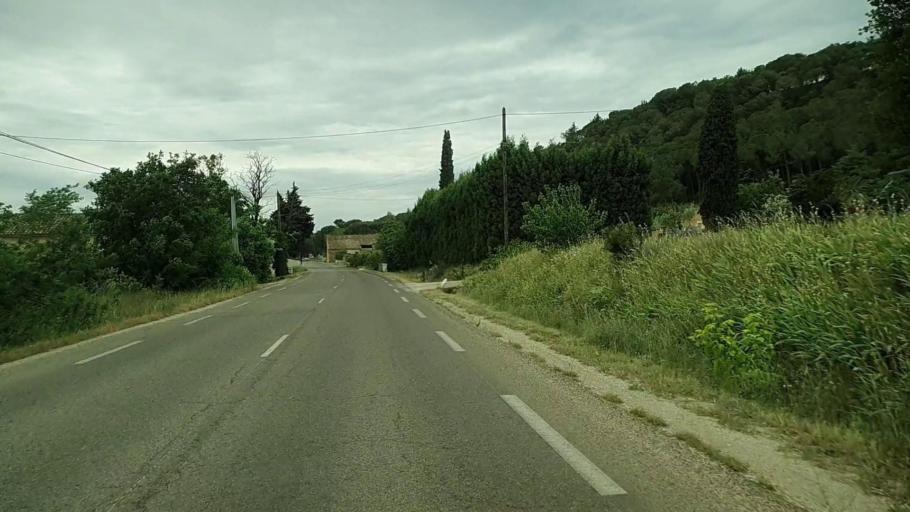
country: FR
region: Languedoc-Roussillon
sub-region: Departement du Gard
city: Tresques
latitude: 44.1264
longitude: 4.6002
